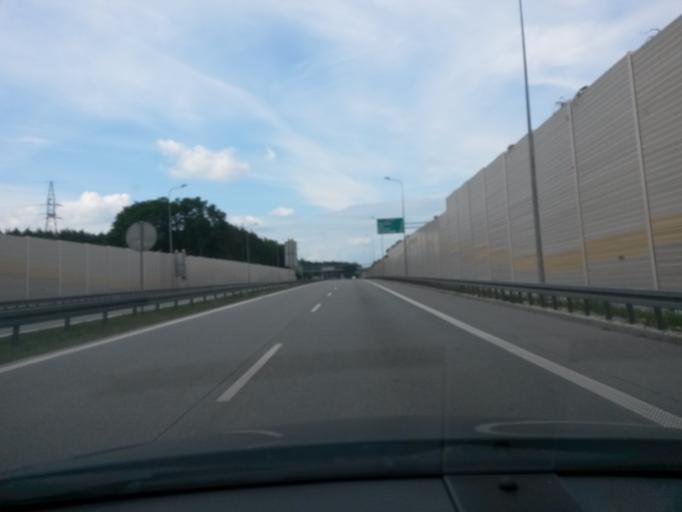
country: PL
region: Lodz Voivodeship
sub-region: Powiat skierniewicki
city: Kowiesy
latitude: 51.9214
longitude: 20.4582
